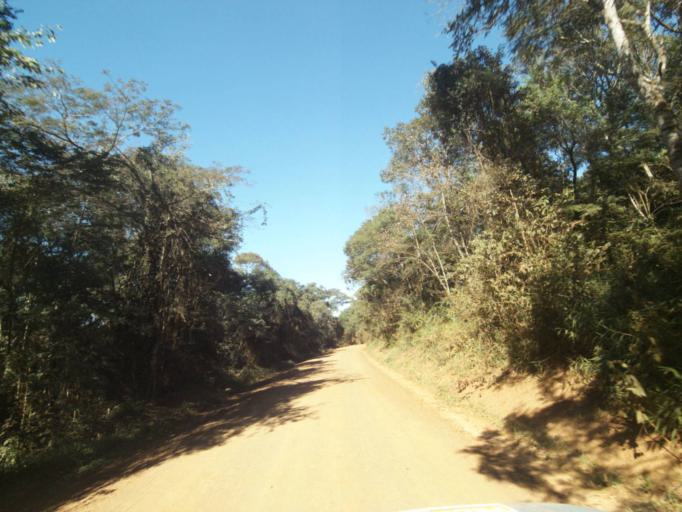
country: BR
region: Parana
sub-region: Tibagi
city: Tibagi
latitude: -24.5781
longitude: -50.6195
